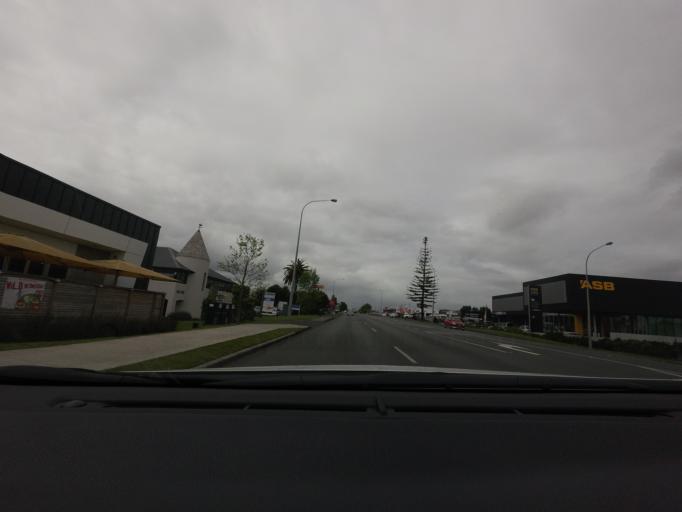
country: NZ
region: Auckland
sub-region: Auckland
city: Rosebank
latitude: -36.8535
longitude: 174.6301
